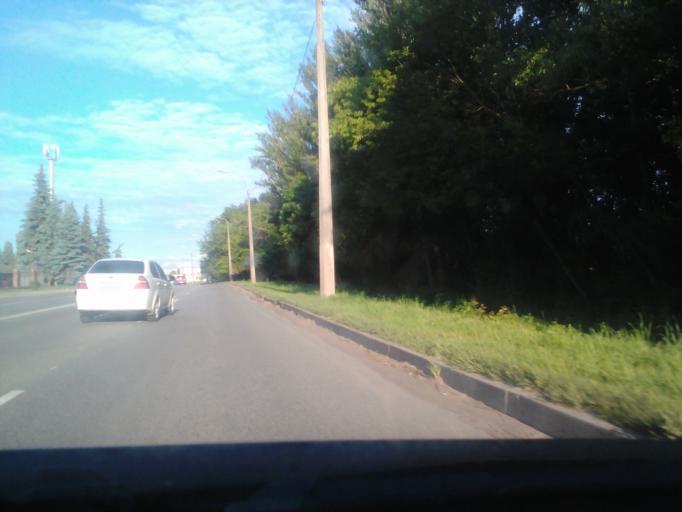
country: RU
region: Kursk
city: Kurchatov
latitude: 51.6568
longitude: 35.6547
